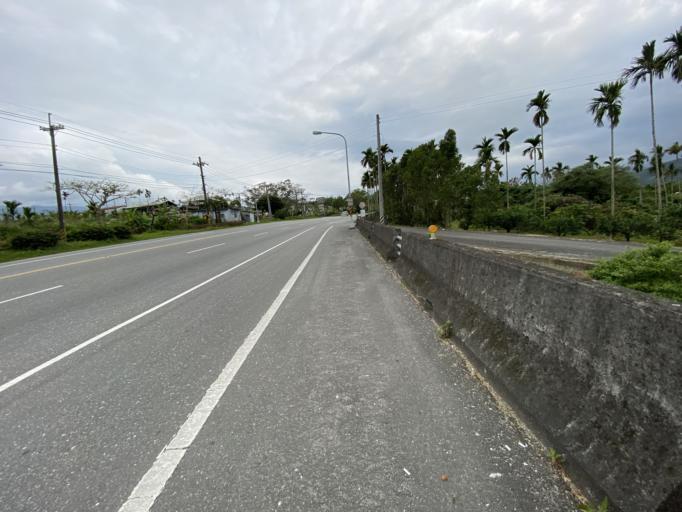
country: TW
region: Taiwan
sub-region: Hualien
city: Hualian
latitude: 23.4696
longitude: 121.3598
